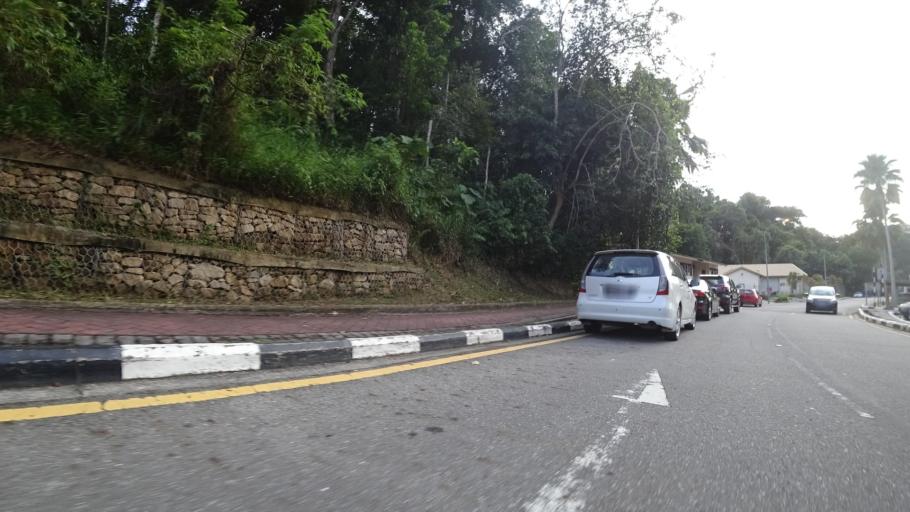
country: BN
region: Brunei and Muara
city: Bandar Seri Begawan
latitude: 4.8996
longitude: 114.9431
